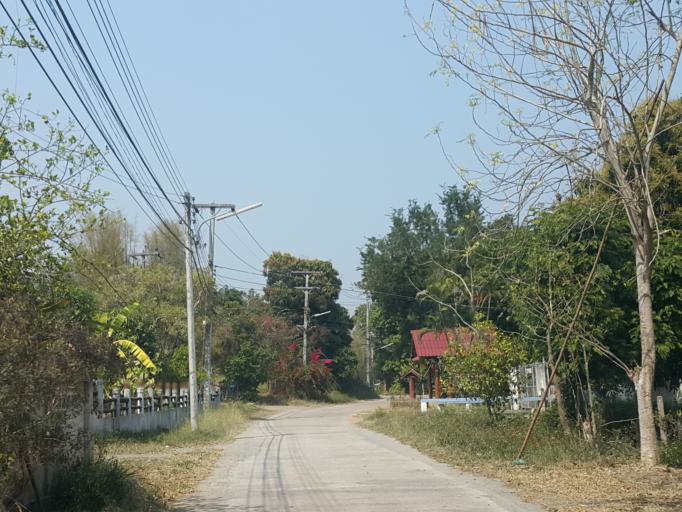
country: TH
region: Chiang Mai
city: San Sai
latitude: 18.9502
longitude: 98.9189
